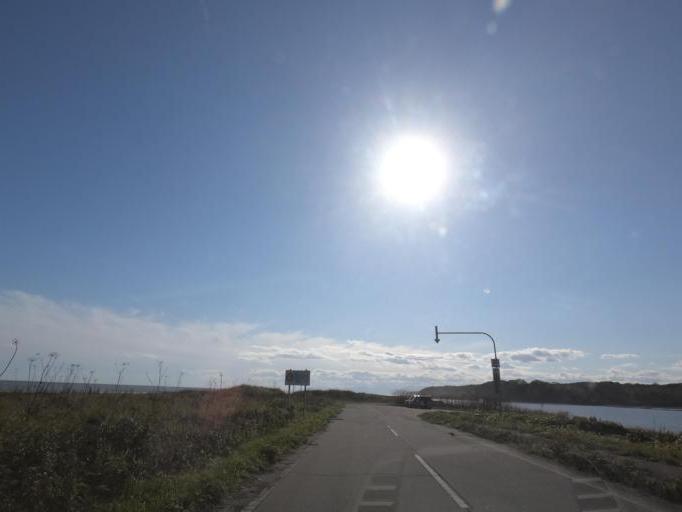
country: JP
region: Hokkaido
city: Obihiro
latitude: 42.5808
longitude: 143.5303
